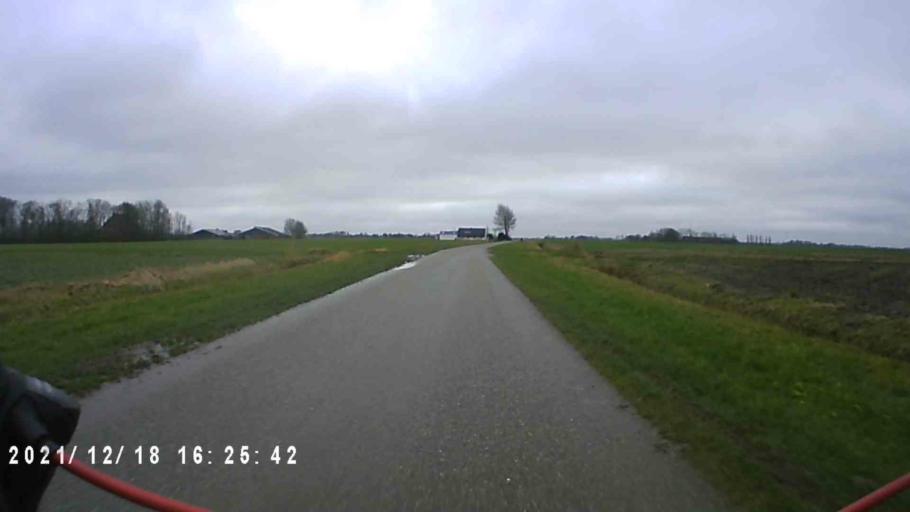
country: NL
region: Friesland
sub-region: Gemeente Dongeradeel
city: Dokkum
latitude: 53.3759
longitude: 6.0366
